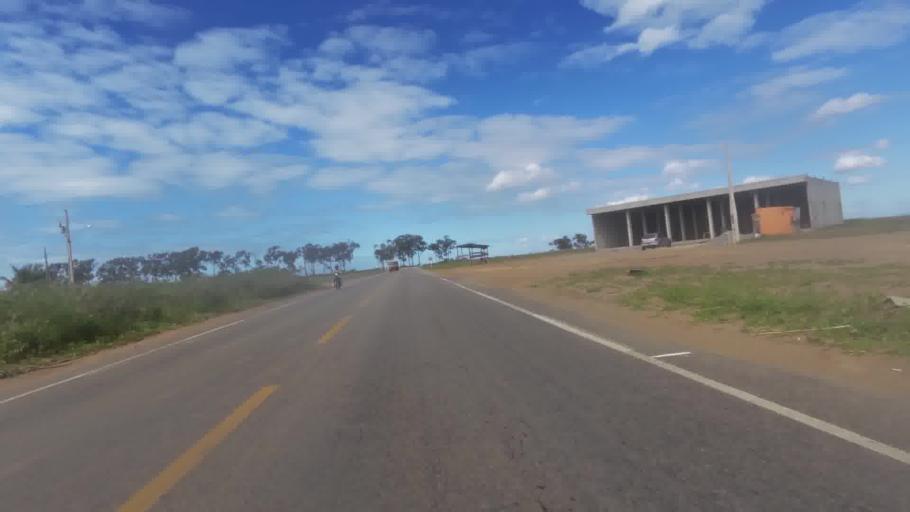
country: BR
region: Espirito Santo
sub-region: Marataizes
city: Marataizes
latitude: -21.0632
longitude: -40.8503
